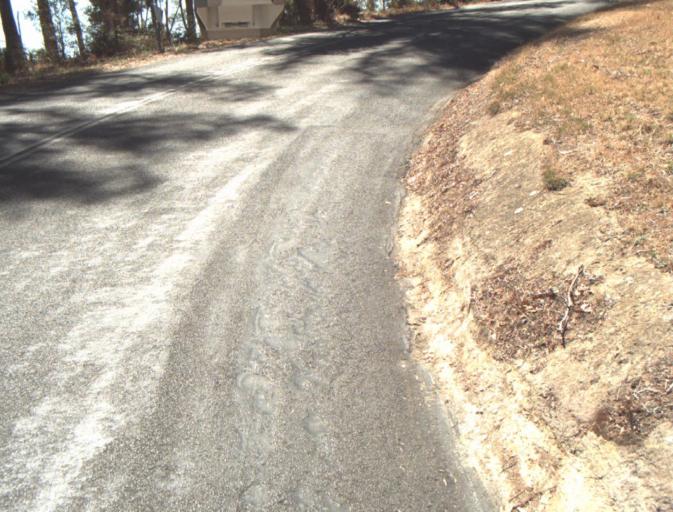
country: AU
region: Tasmania
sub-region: Launceston
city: Mayfield
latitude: -41.2569
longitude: 147.1372
